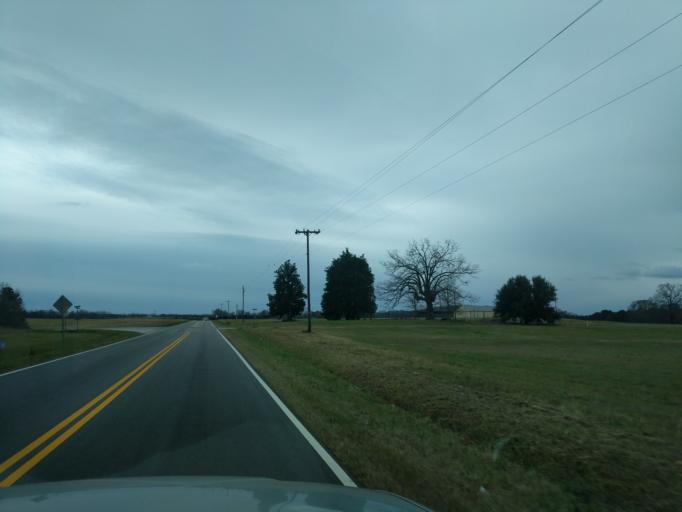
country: US
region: South Carolina
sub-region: Laurens County
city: Laurens
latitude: 34.3704
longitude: -81.9938
